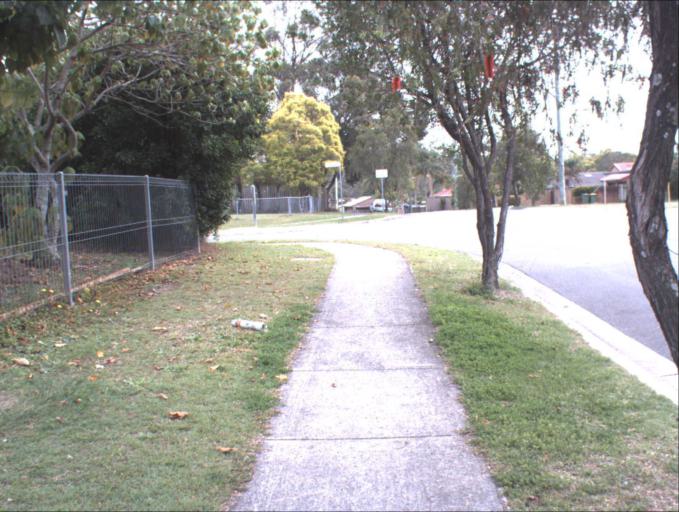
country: AU
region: Queensland
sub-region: Logan
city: Woodridge
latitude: -27.6587
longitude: 153.0598
